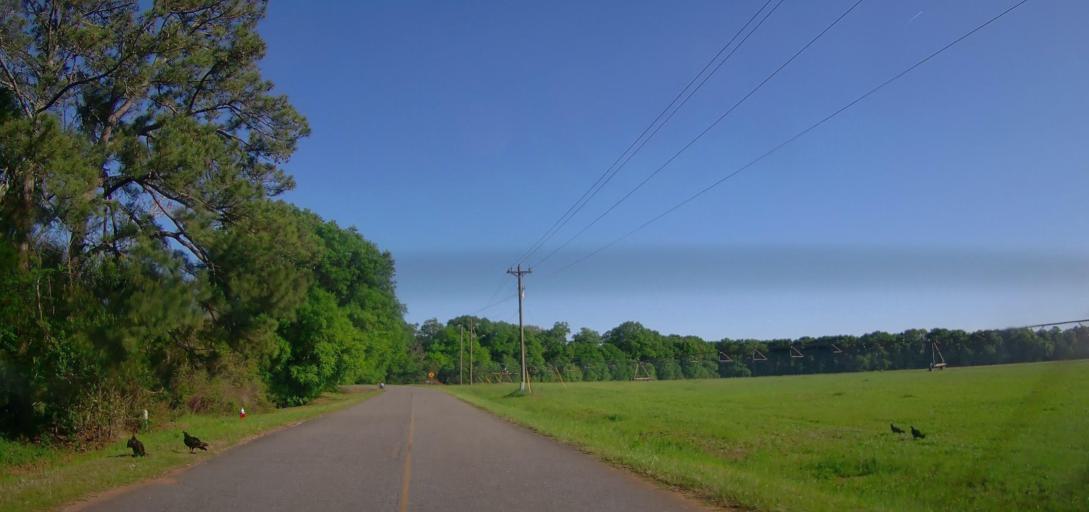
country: US
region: Georgia
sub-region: Houston County
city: Perry
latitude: 32.4213
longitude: -83.7766
